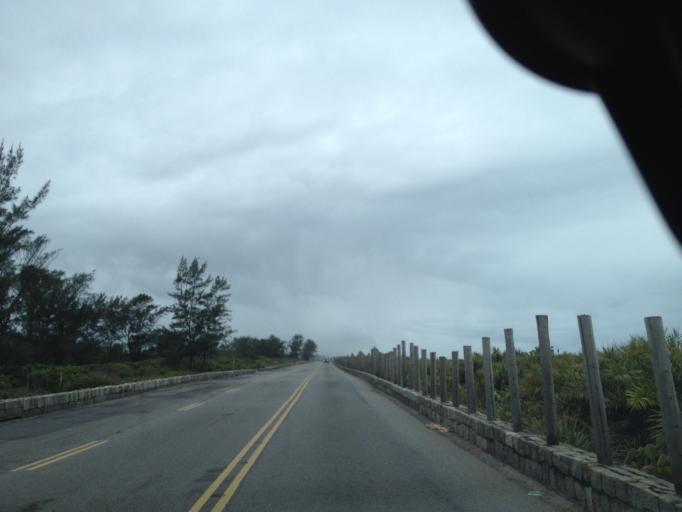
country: BR
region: Rio de Janeiro
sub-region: Nilopolis
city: Nilopolis
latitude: -23.0175
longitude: -43.4236
